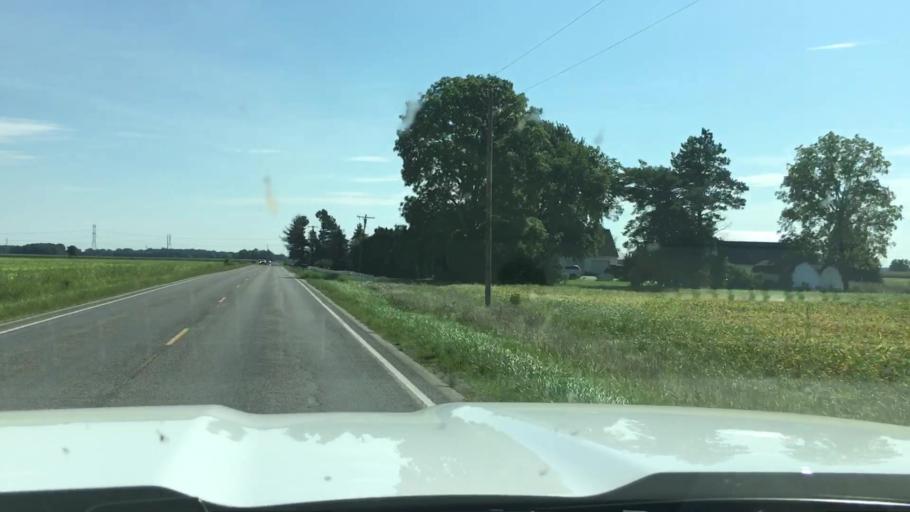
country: US
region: Michigan
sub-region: Saginaw County
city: Freeland
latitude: 43.5253
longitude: -84.1979
